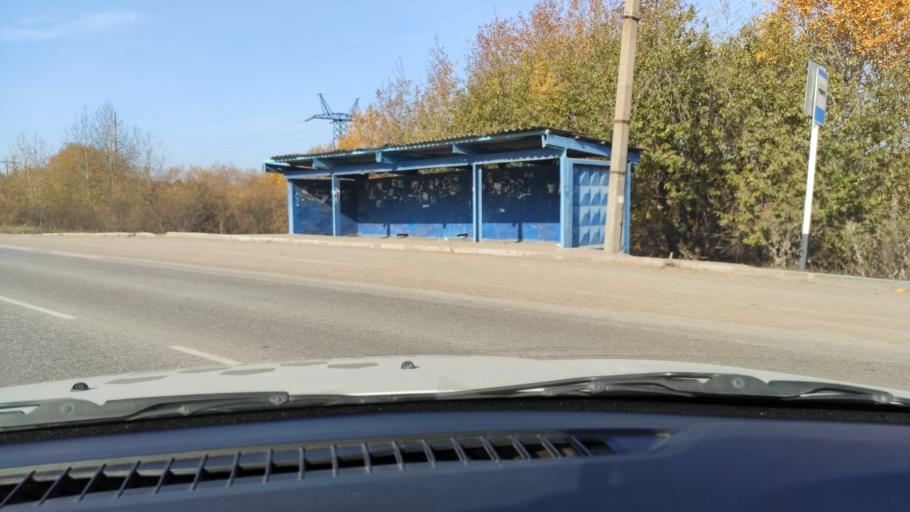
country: RU
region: Perm
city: Sylva
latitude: 58.0266
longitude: 56.7325
